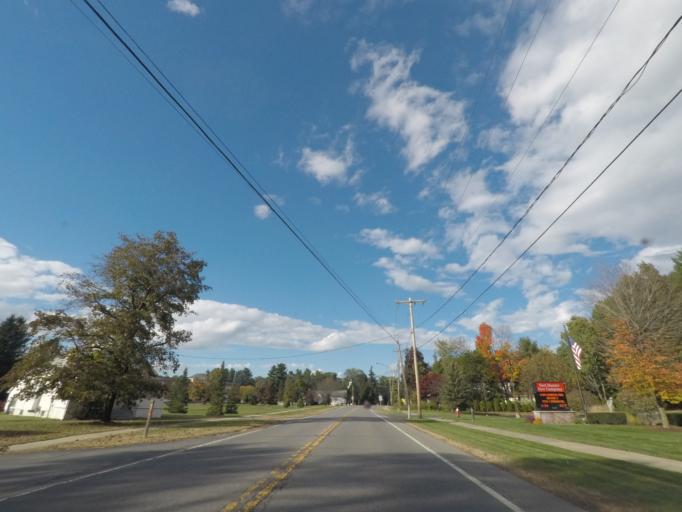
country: US
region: New York
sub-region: Schenectady County
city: Rotterdam
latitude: 42.7402
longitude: -73.9421
